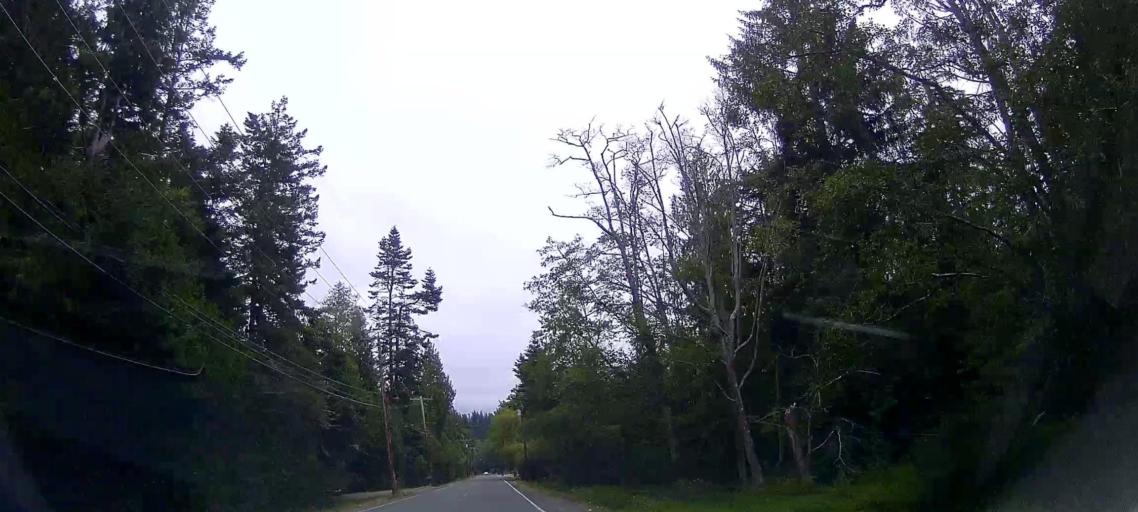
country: US
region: Washington
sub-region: Skagit County
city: Anacortes
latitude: 48.4516
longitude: -122.6481
